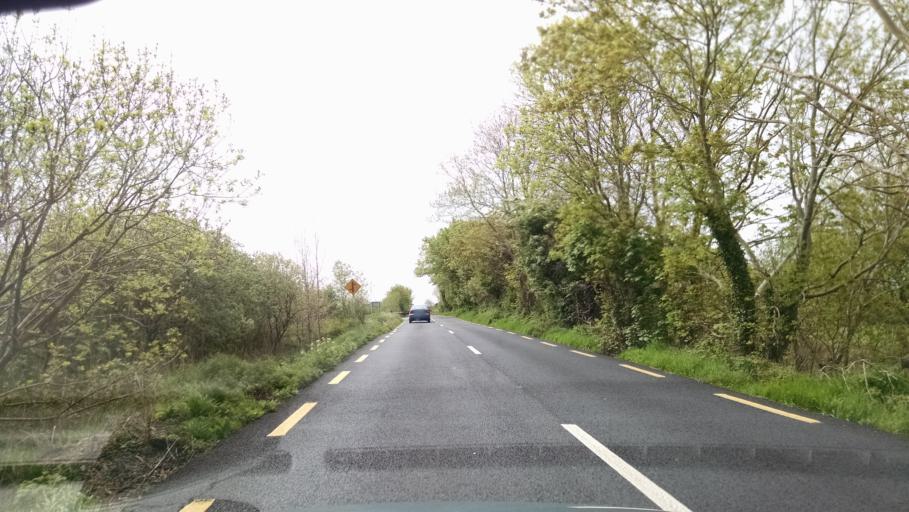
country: IE
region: Connaught
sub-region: County Galway
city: Claregalway
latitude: 53.3883
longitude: -9.0168
